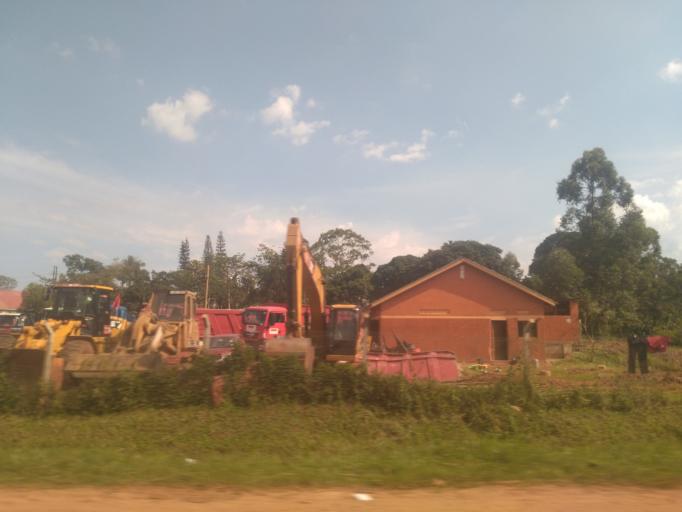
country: UG
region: Central Region
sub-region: Wakiso District
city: Kajansi
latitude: 0.2818
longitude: 32.4843
